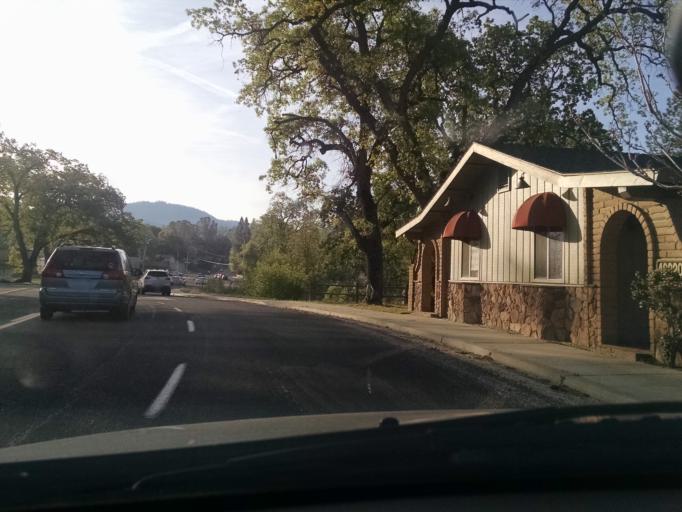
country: US
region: California
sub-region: Madera County
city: Oakhurst
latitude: 37.3291
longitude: -119.6501
